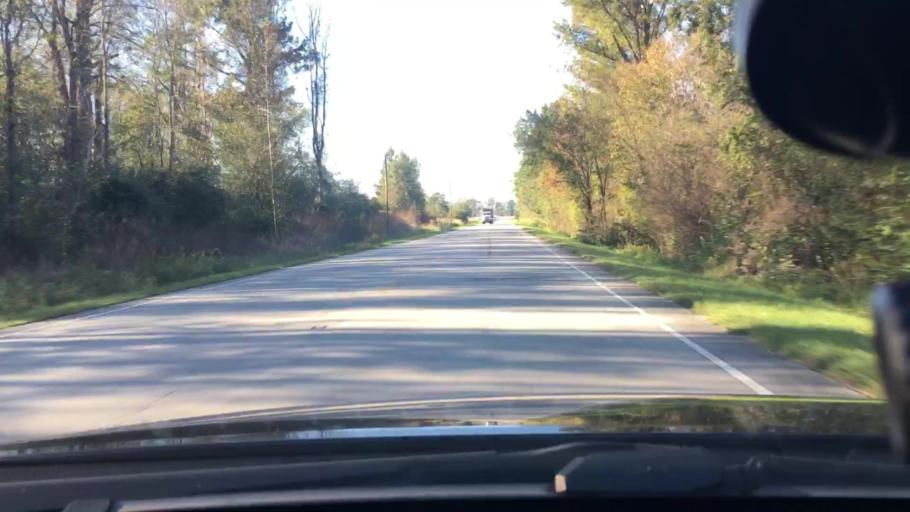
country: US
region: North Carolina
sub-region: Craven County
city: Vanceboro
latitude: 35.3686
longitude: -77.2049
